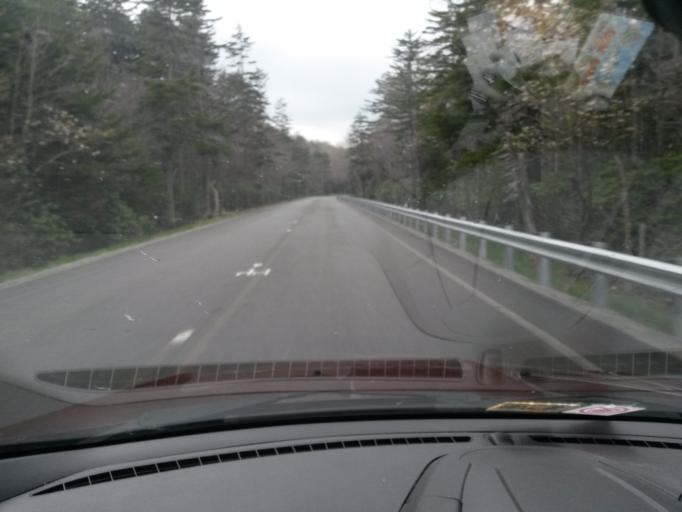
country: US
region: West Virginia
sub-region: Randolph County
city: Elkins
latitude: 38.6234
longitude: -79.8931
